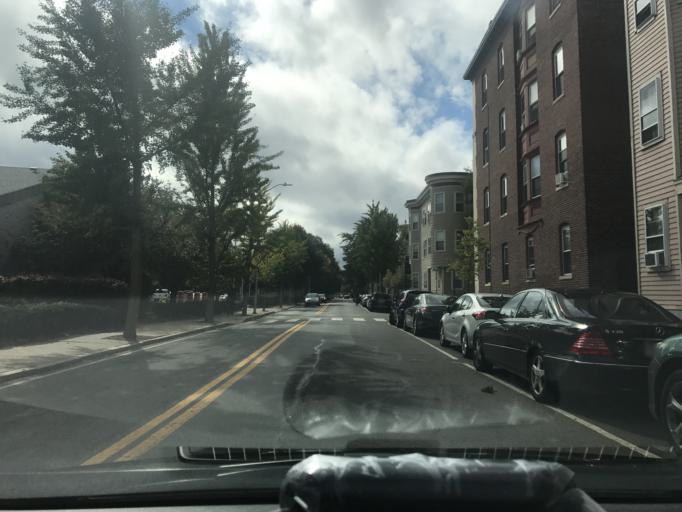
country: US
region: Massachusetts
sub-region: Middlesex County
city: Cambridge
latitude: 42.3716
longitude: -71.0888
